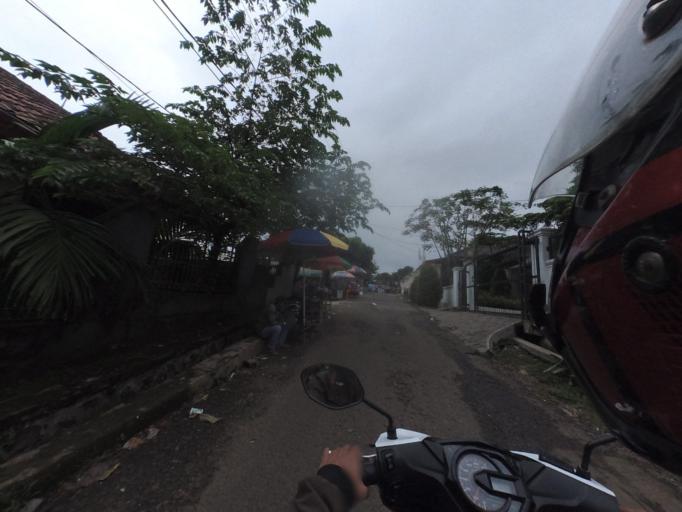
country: ID
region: West Java
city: Bogor
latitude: -6.6379
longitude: 106.7344
